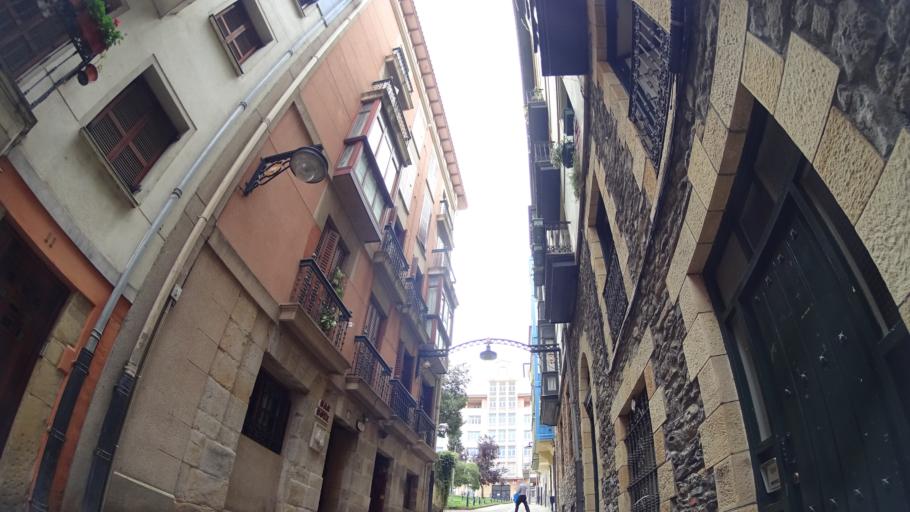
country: ES
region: Basque Country
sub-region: Bizkaia
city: Portugalete
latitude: 43.3206
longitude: -3.0174
